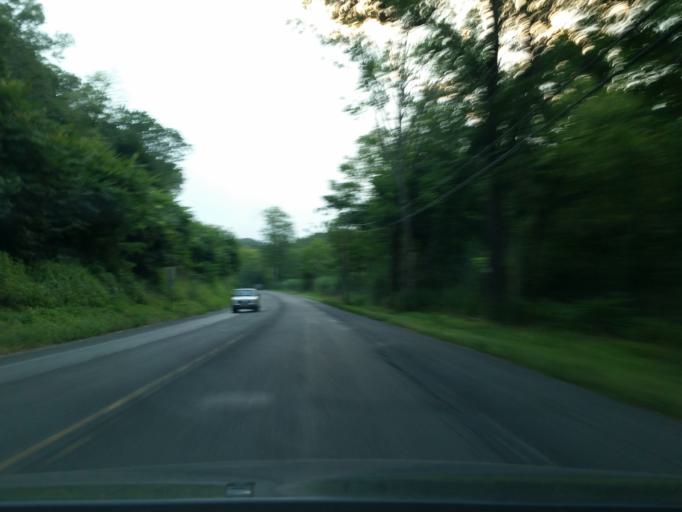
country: US
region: Pennsylvania
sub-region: Lebanon County
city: Sand Hill
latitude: 40.3519
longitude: -76.4371
